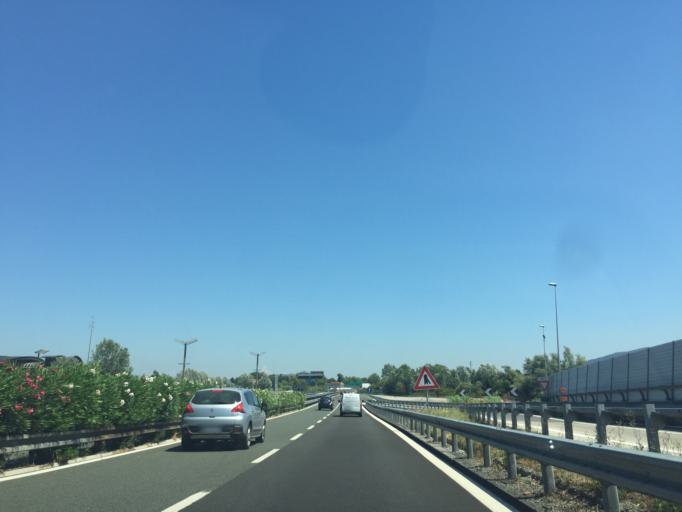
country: IT
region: Tuscany
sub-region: Provincia di Lucca
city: Lucca
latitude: 43.8372
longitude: 10.4669
